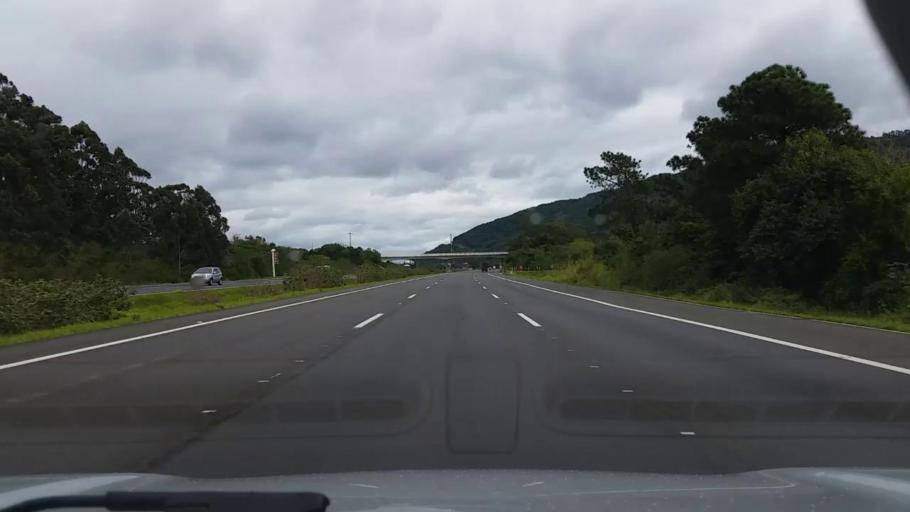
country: BR
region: Rio Grande do Sul
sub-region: Osorio
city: Osorio
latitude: -29.8978
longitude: -50.3190
